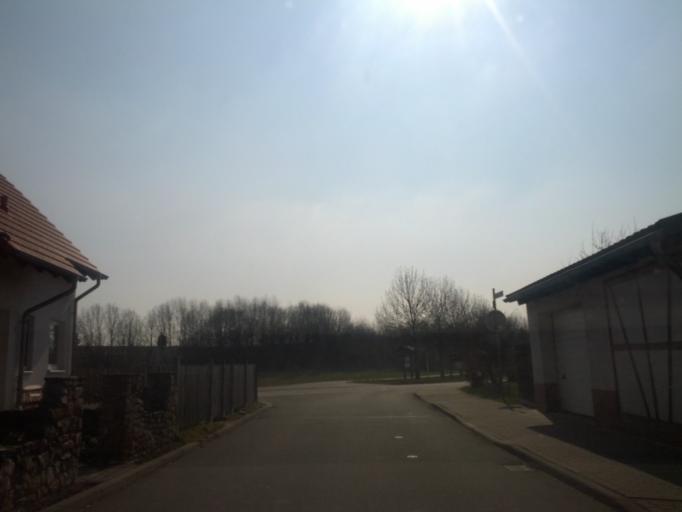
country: DE
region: Thuringia
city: Apfelstadt
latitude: 50.9007
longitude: 10.8904
